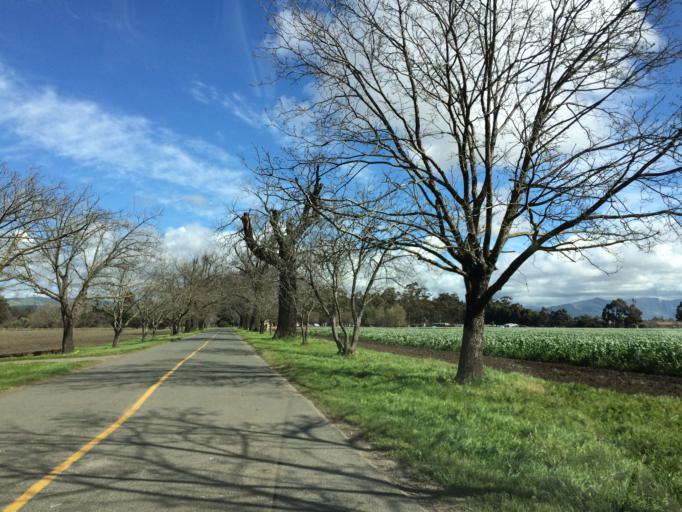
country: US
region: California
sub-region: Alameda County
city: Newark
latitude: 37.5554
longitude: -122.0551
